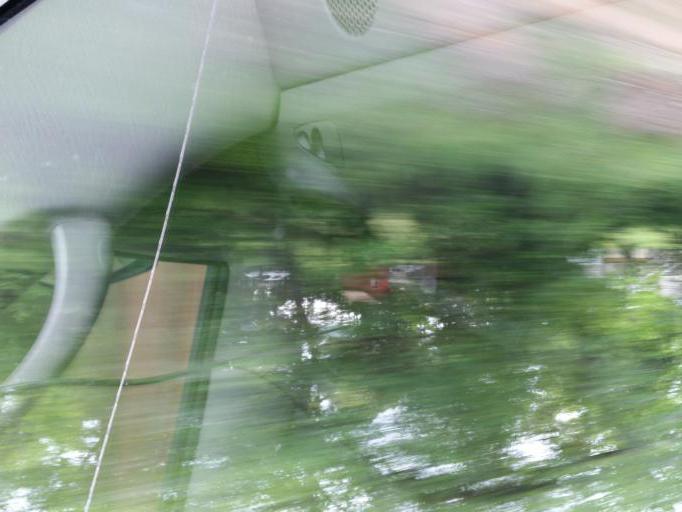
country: US
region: Georgia
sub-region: Crawford County
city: Knoxville
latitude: 32.6746
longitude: -83.9000
